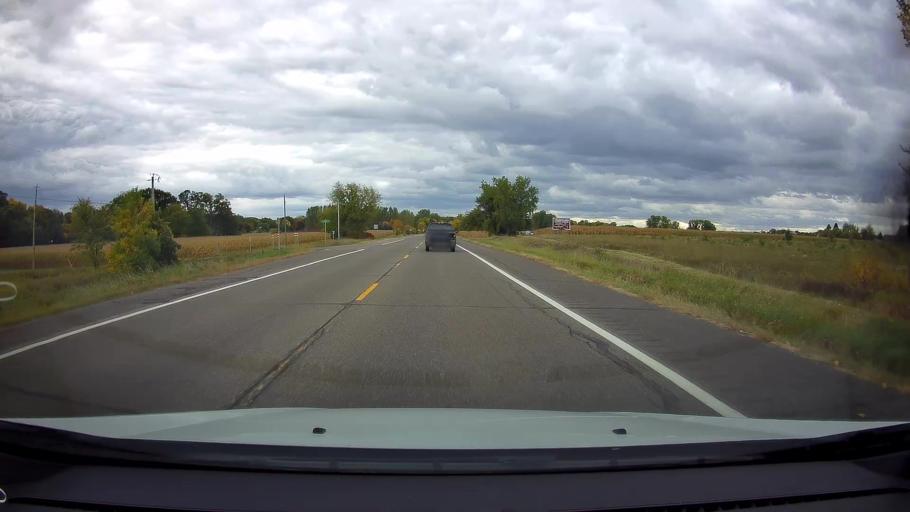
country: US
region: Minnesota
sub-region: Chisago County
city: Chisago City
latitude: 45.3497
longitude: -92.9117
